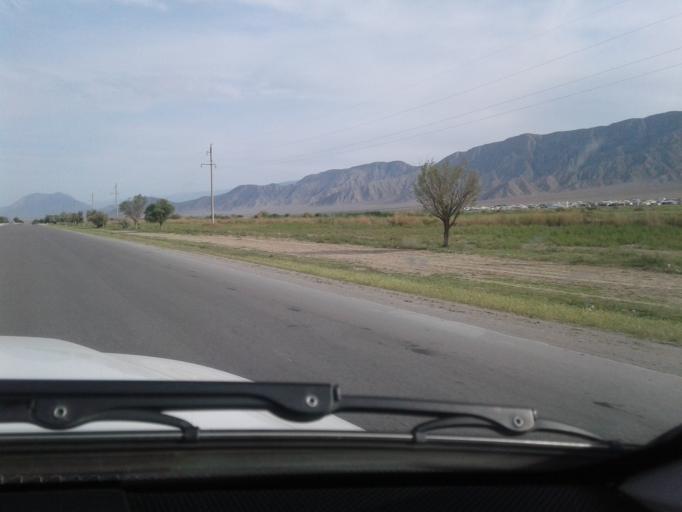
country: TM
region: Ahal
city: Arcabil
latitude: 38.1973
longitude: 57.8305
